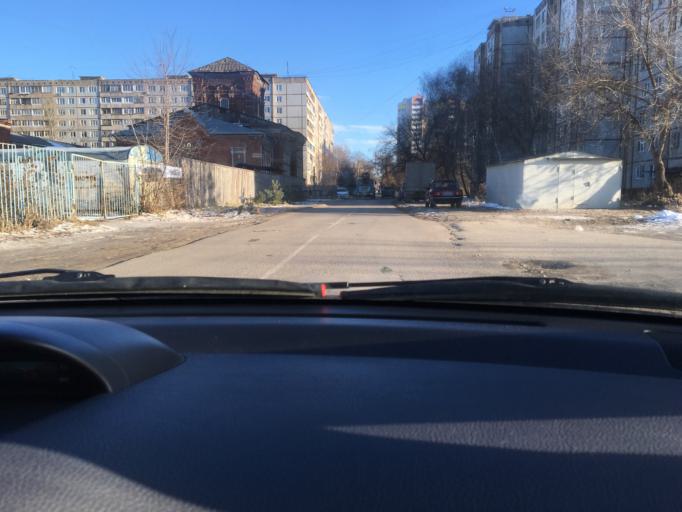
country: RU
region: Tula
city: Tula
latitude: 54.2144
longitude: 37.5985
